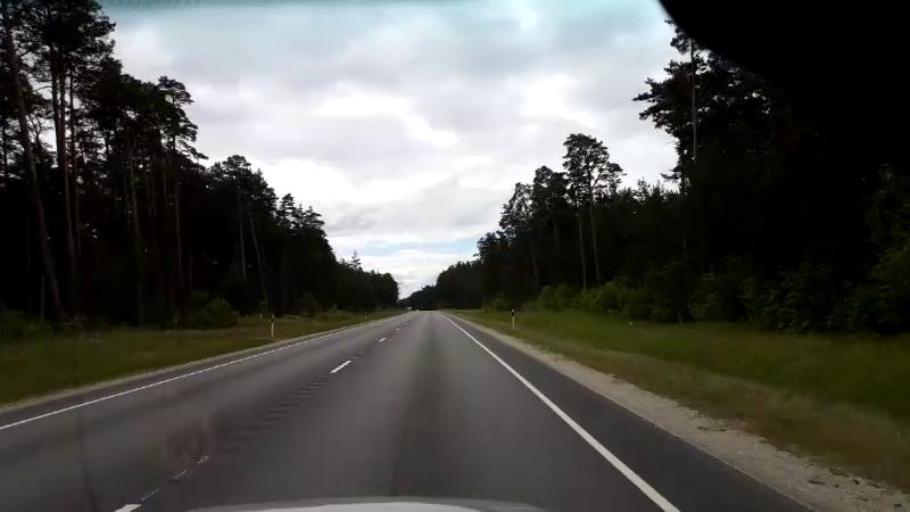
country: EE
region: Paernumaa
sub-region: Paernu linn
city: Parnu
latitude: 58.1760
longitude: 24.4937
